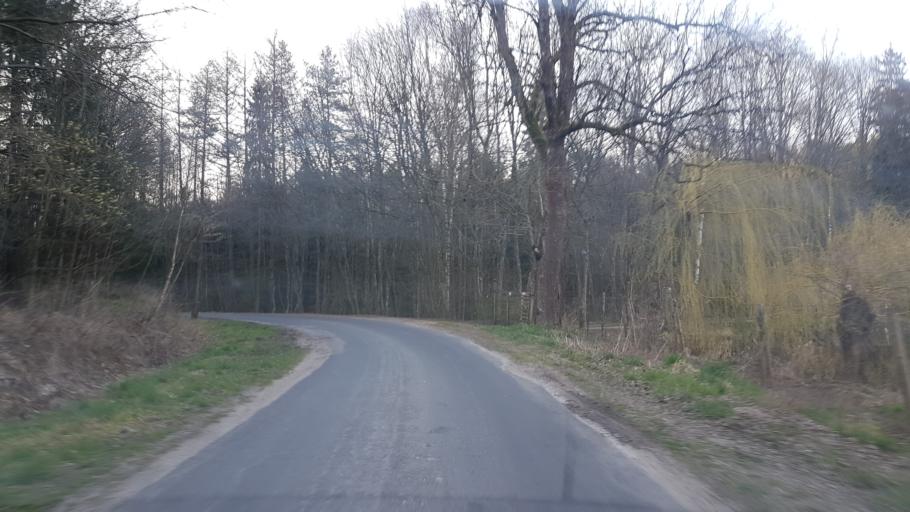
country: PL
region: West Pomeranian Voivodeship
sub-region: Powiat swidwinski
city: Swidwin
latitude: 53.7332
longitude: 15.7265
